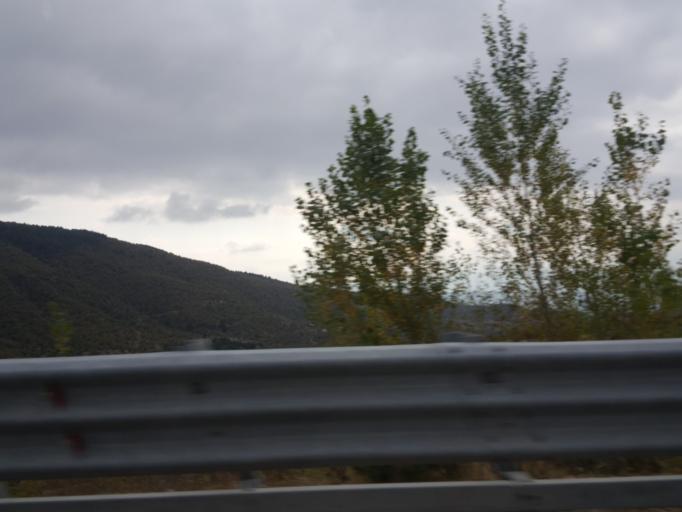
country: TR
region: Corum
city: Kargi
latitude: 41.1782
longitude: 34.5483
